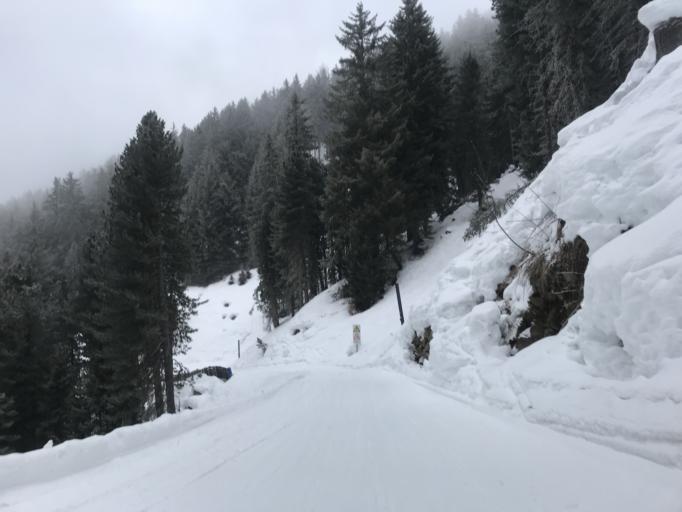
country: IT
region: Trentino-Alto Adige
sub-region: Bolzano
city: San Pietro
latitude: 46.6875
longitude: 11.7028
